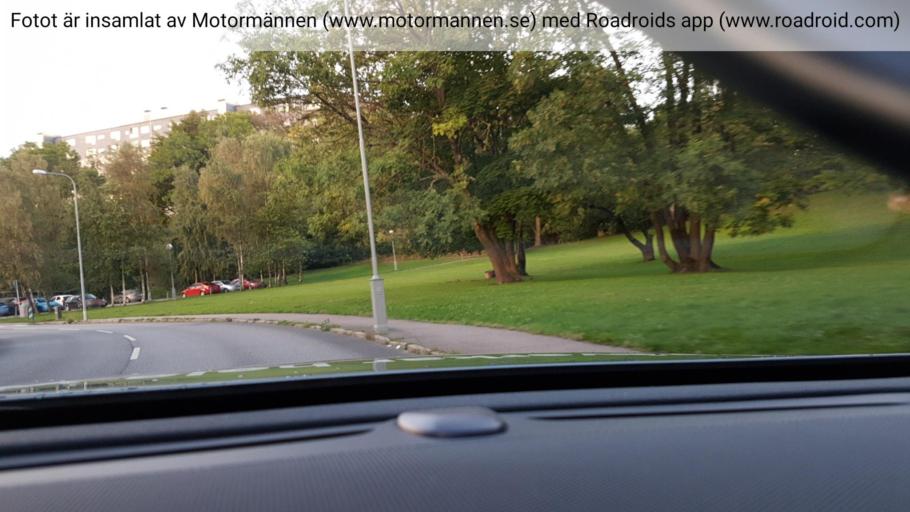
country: SE
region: Vaestra Goetaland
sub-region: Molndal
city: Moelndal
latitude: 57.6817
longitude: 11.9964
